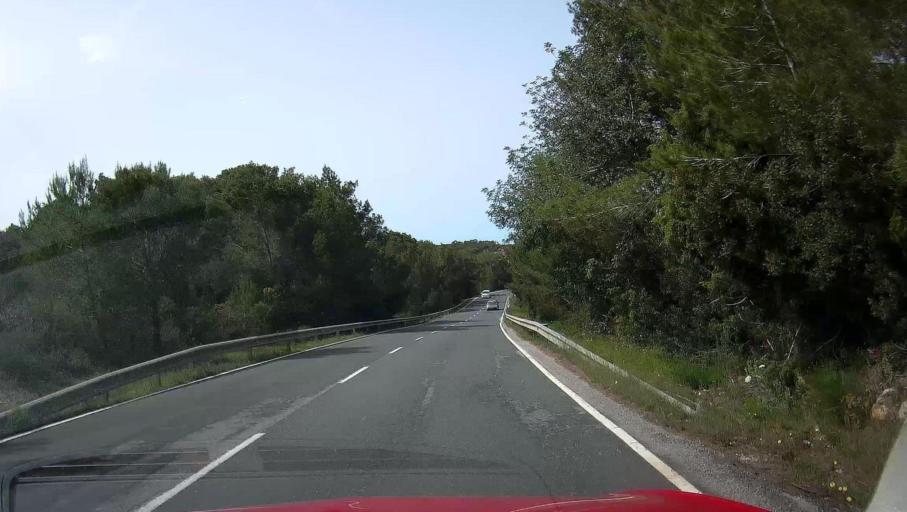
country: ES
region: Balearic Islands
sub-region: Illes Balears
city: Sant Joan de Labritja
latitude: 39.0941
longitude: 1.4992
